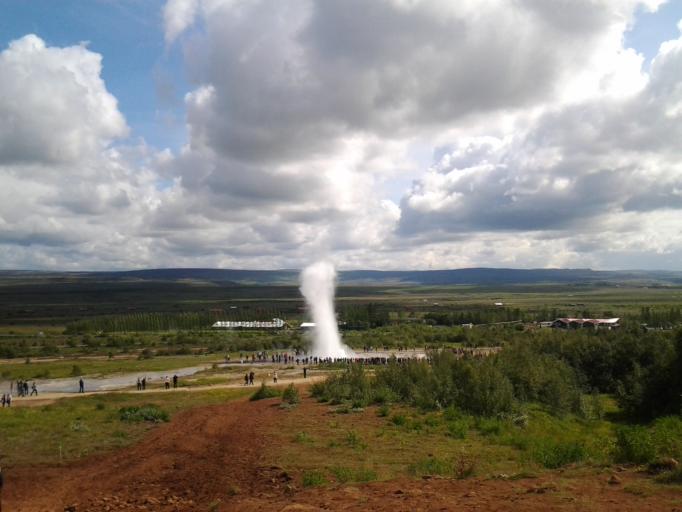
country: IS
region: South
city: Selfoss
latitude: 64.3139
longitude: -20.3031
